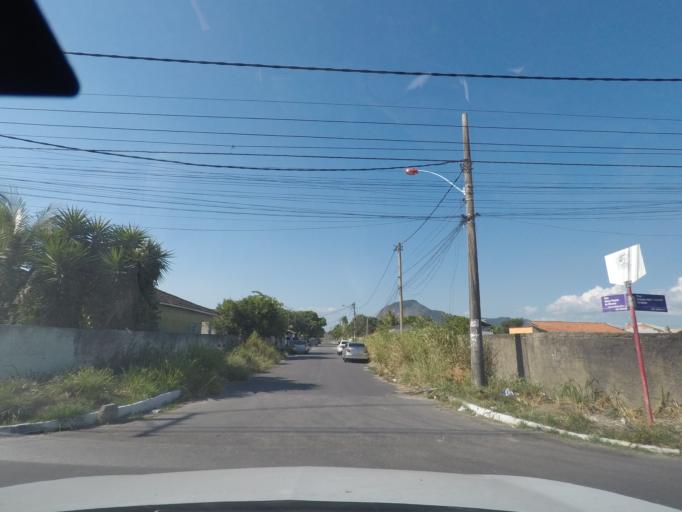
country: BR
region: Rio de Janeiro
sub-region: Marica
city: Marica
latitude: -22.9670
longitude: -42.9217
